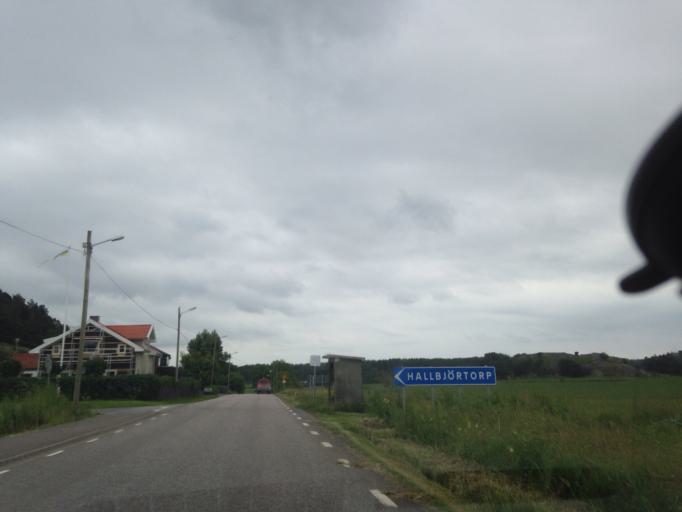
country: SE
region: Vaestra Goetaland
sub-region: Kungalvs Kommun
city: Kode
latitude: 57.8411
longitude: 11.7936
